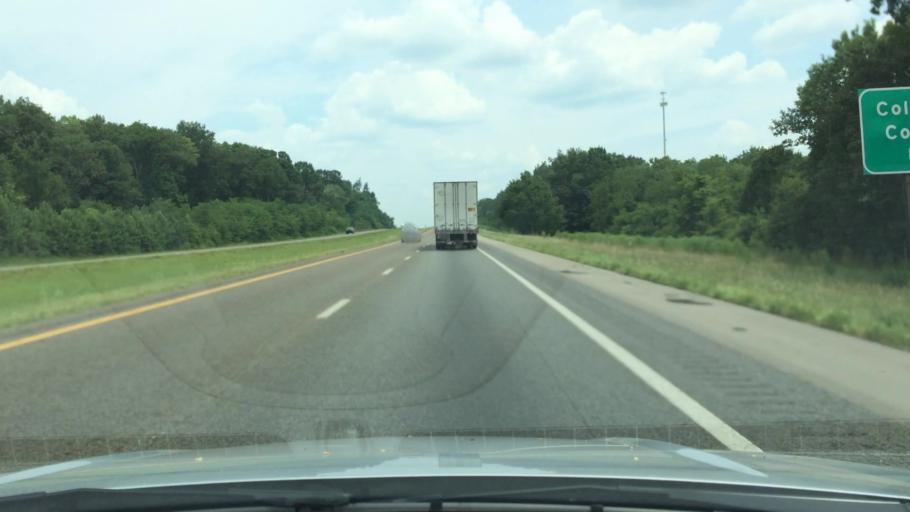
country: US
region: Tennessee
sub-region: Maury County
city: Spring Hill
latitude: 35.6305
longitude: -86.8962
